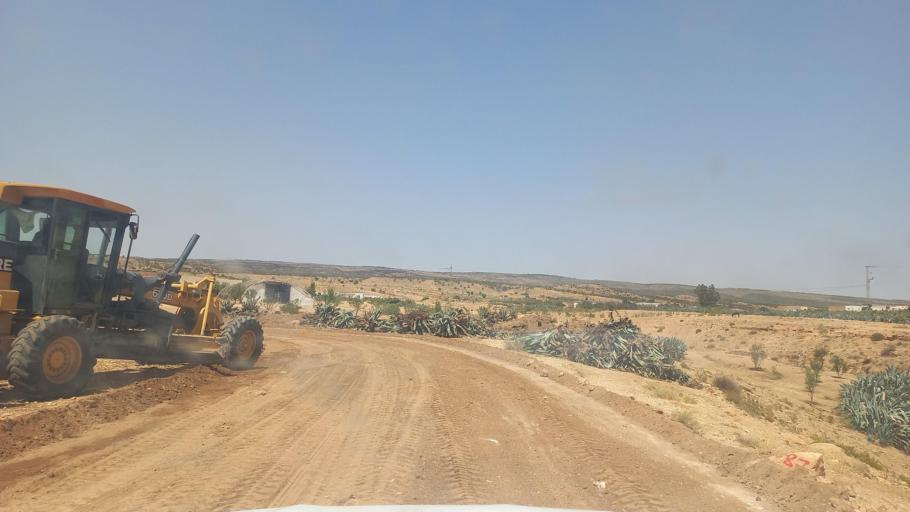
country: TN
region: Al Qasrayn
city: Kasserine
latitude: 35.2975
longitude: 8.9402
